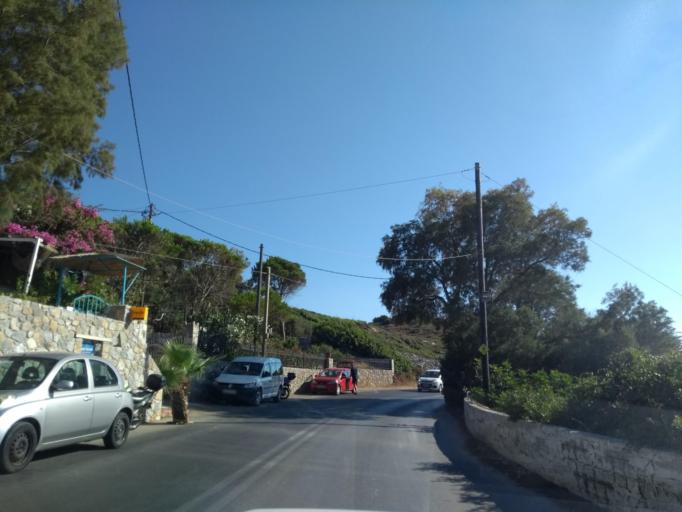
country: GR
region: Crete
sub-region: Nomos Chanias
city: Pithari
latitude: 35.5528
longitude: 24.0863
